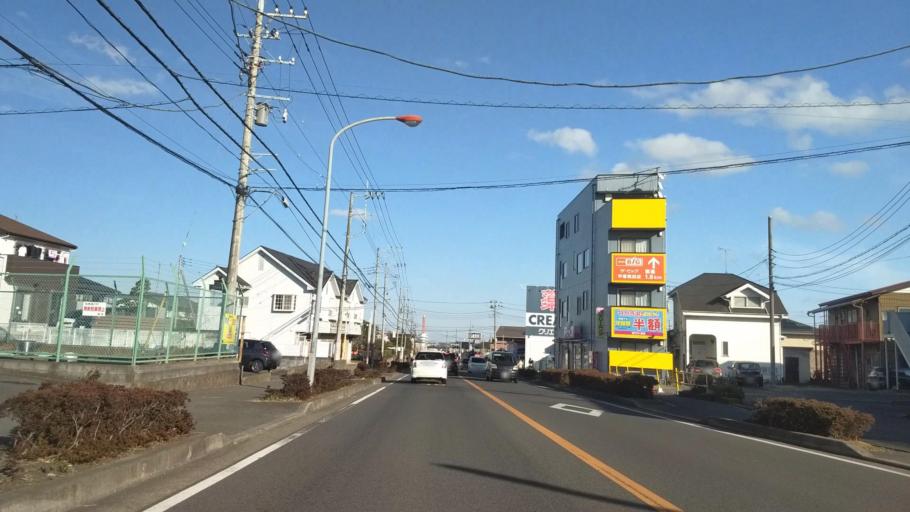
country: JP
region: Kanagawa
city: Hadano
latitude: 35.3632
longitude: 139.2642
